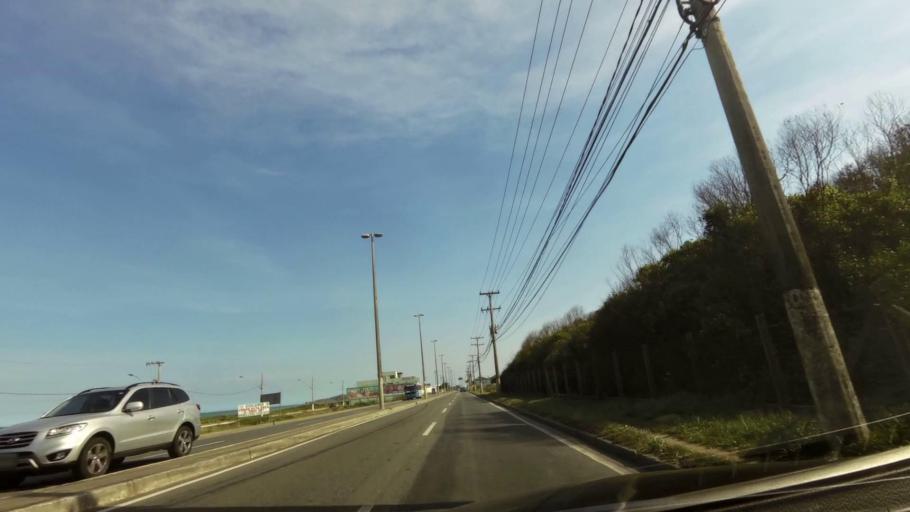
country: BR
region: Espirito Santo
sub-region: Vila Velha
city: Vila Velha
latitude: -20.3877
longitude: -40.3130
